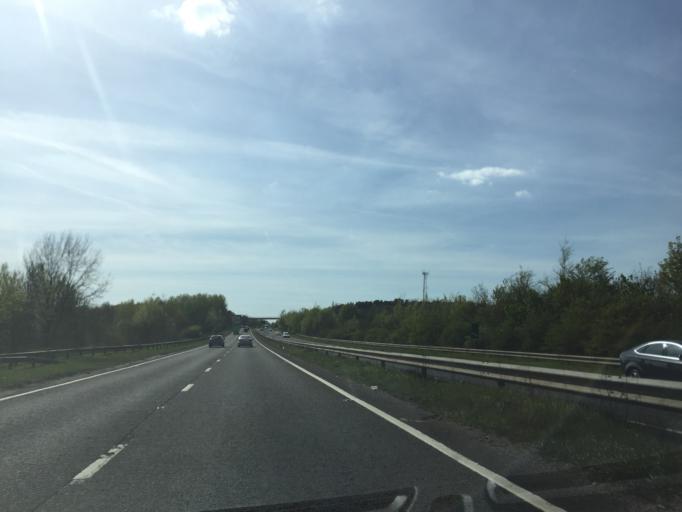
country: GB
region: England
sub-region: Greater London
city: Bexley
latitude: 51.4094
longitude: 0.1390
